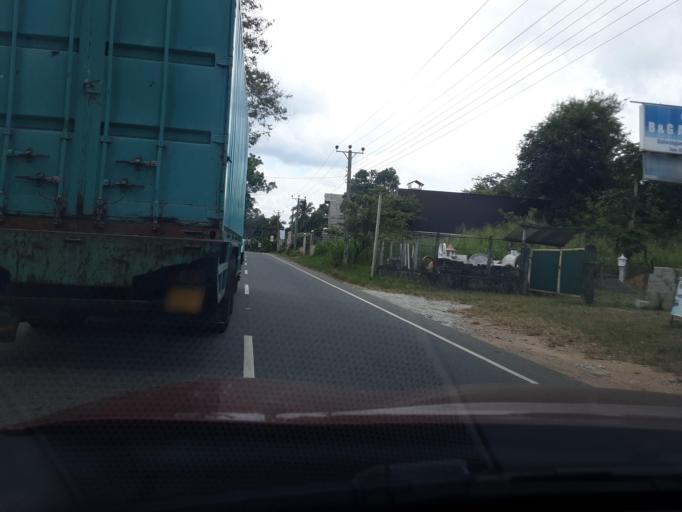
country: LK
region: North Western
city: Kurunegala
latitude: 7.4453
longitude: 80.2041
